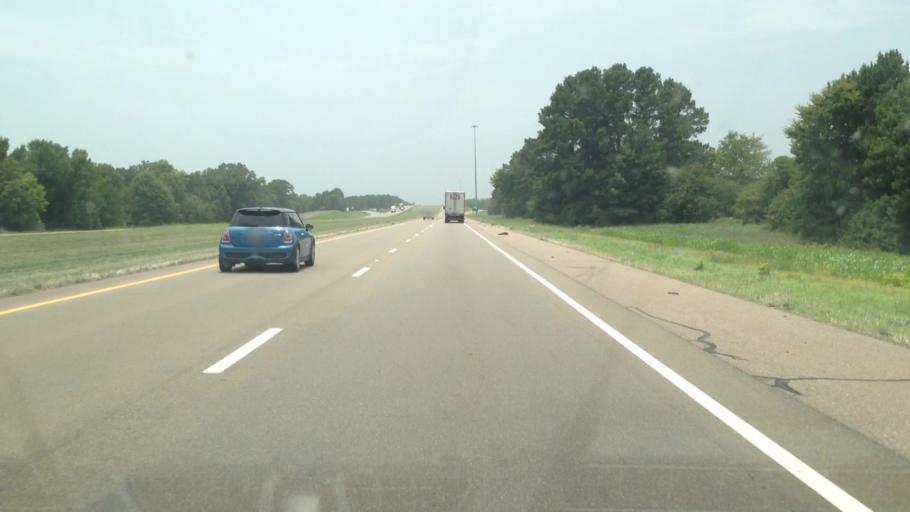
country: US
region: Texas
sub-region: Bowie County
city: De Kalb
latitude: 33.4218
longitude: -94.5498
